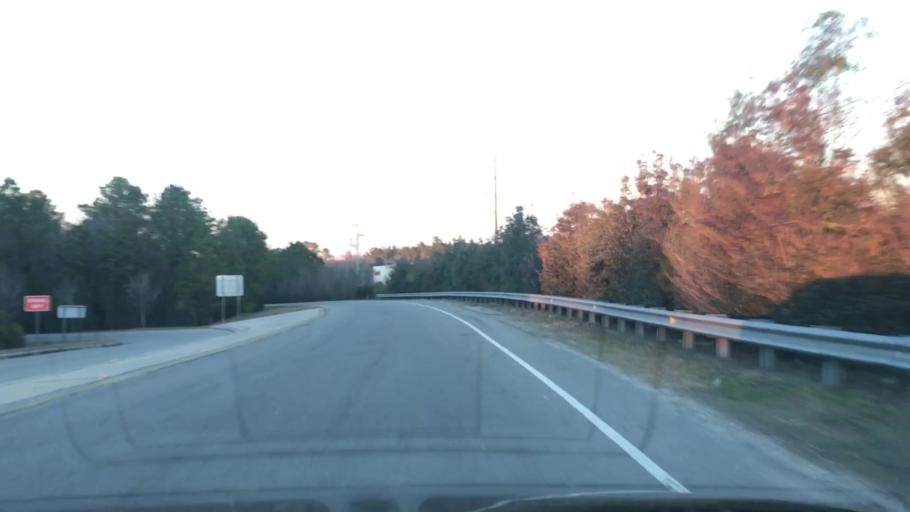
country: US
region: North Carolina
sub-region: Brunswick County
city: Shallotte
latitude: 33.9756
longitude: -78.4028
